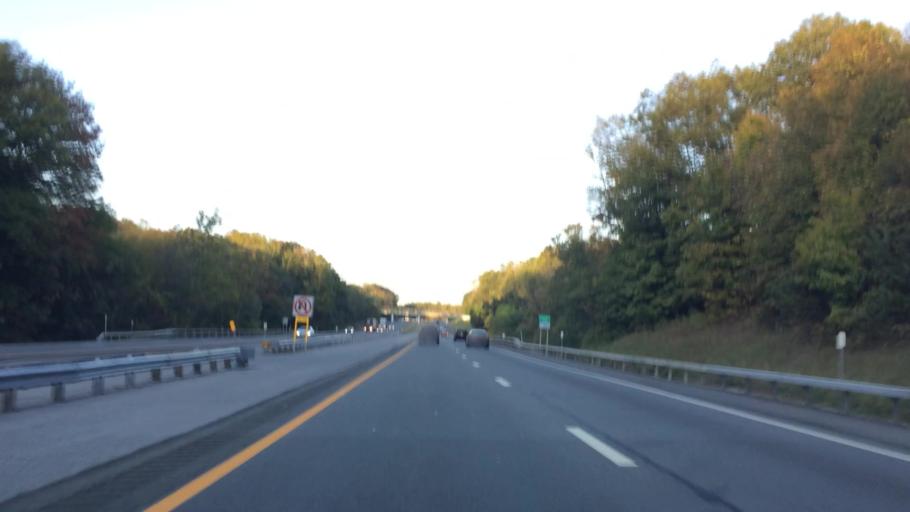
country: US
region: New York
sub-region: Orange County
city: Firthcliffe
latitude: 41.4083
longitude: -74.0780
